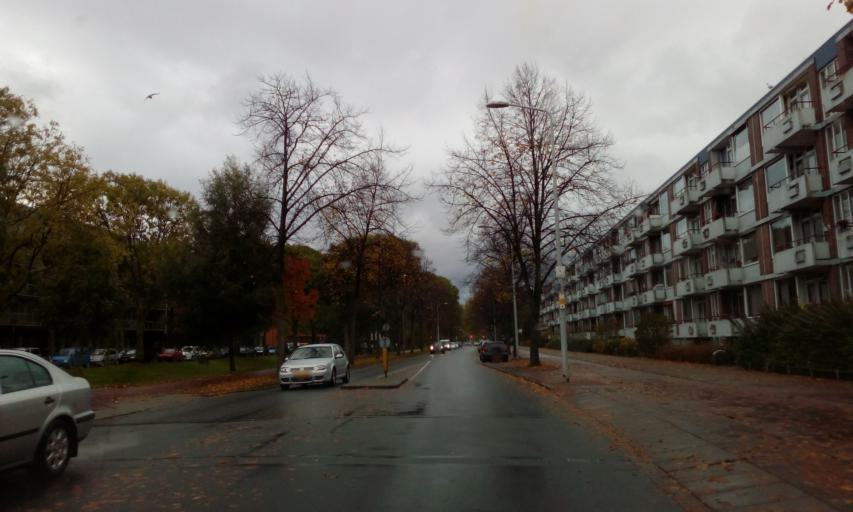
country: NL
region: South Holland
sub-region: Gemeente Westland
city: Kwintsheul
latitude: 52.0488
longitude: 4.2710
